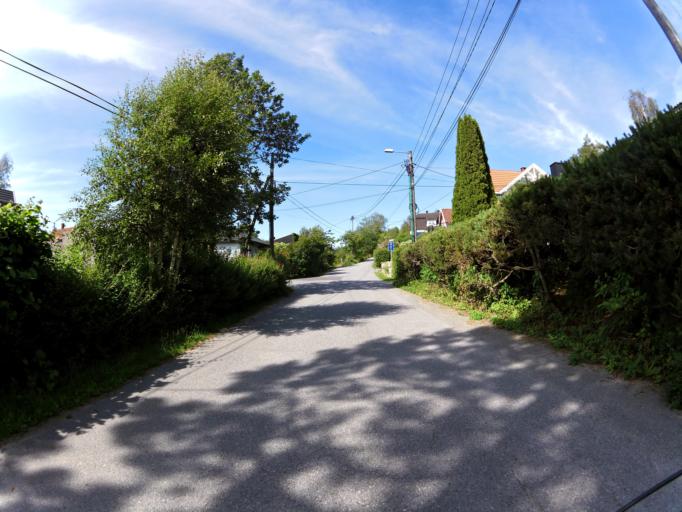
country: NO
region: Ostfold
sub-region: Fredrikstad
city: Fredrikstad
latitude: 59.2257
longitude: 10.9427
